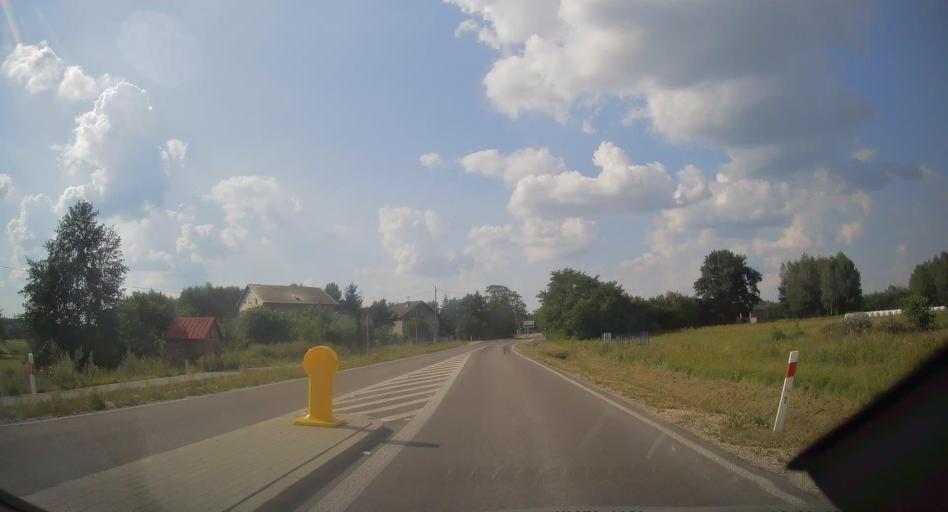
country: PL
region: Swietokrzyskie
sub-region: Powiat konecki
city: Radoszyce
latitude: 51.0612
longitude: 20.2763
